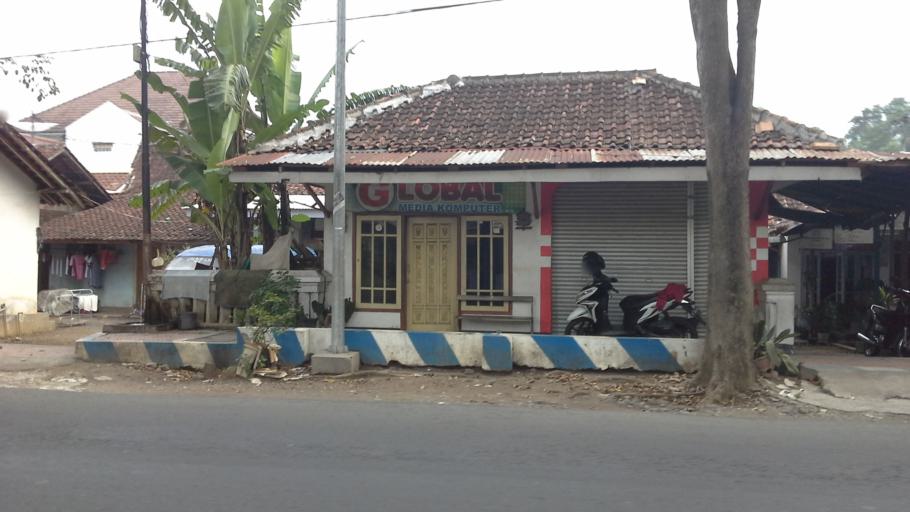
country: ID
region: East Java
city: Bondowoso
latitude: -7.9306
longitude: 113.8206
